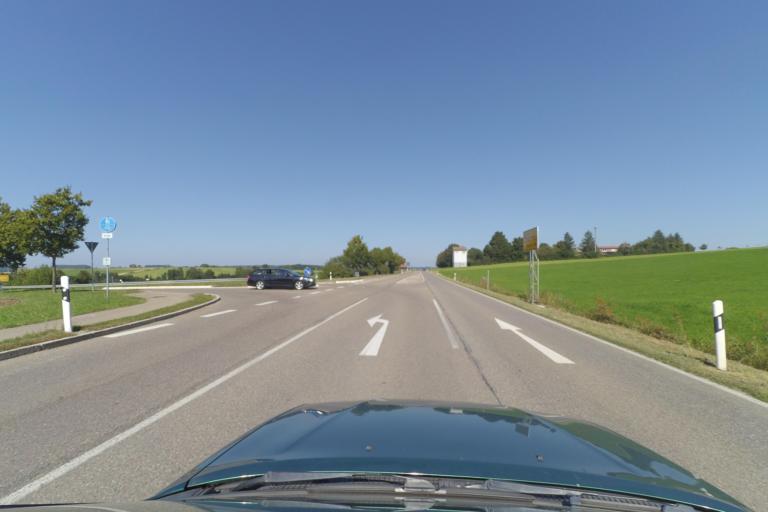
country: DE
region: Baden-Wuerttemberg
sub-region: Regierungsbezirk Stuttgart
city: Heubach
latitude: 48.8037
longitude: 9.9433
